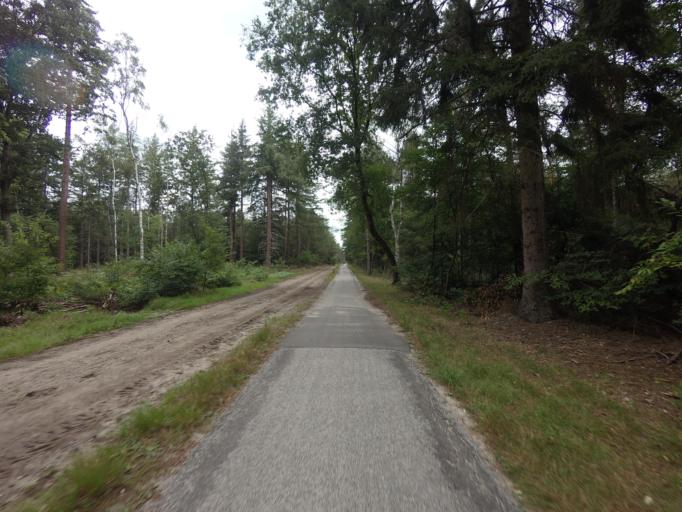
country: NL
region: Overijssel
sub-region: Gemeente Hof van Twente
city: Markelo
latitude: 52.3066
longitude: 6.4531
